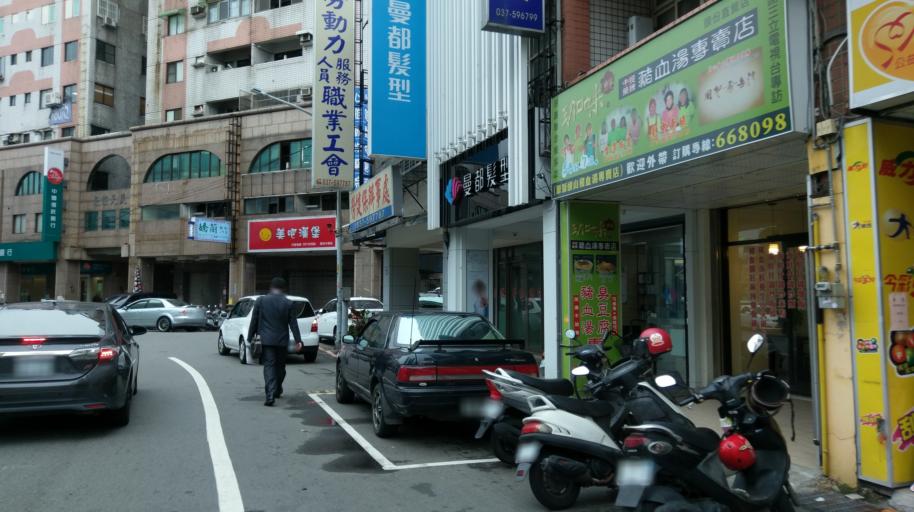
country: TW
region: Taiwan
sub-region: Hsinchu
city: Hsinchu
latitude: 24.6852
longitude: 120.9064
